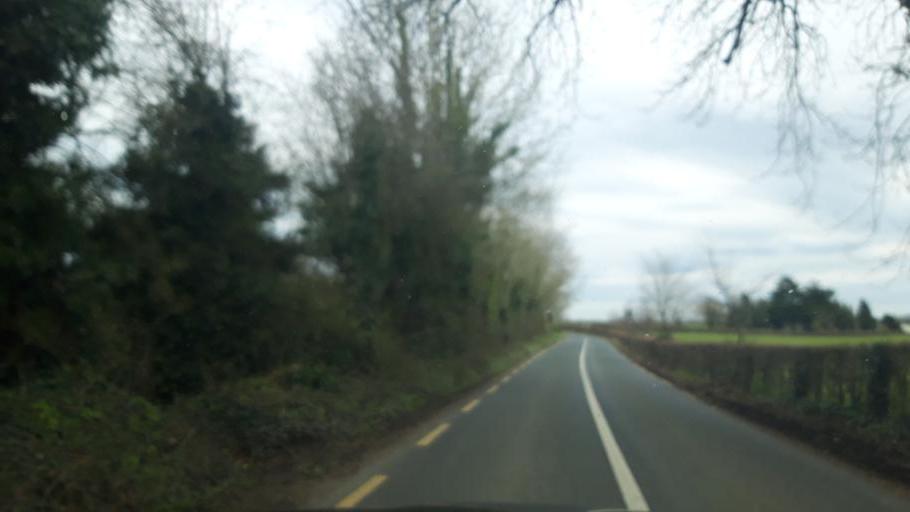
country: IE
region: Leinster
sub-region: Kildare
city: Rathangan
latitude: 53.2496
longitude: -6.9509
